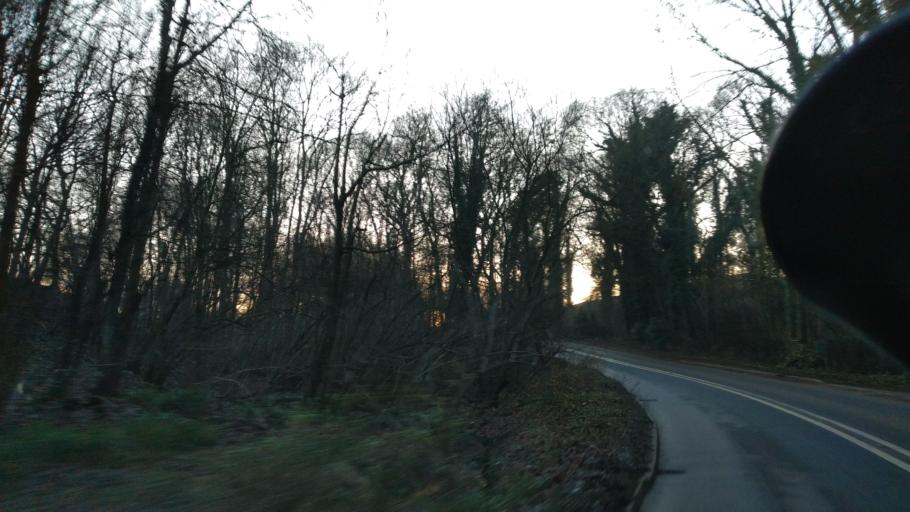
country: GB
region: England
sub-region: Wiltshire
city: Calne
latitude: 51.4098
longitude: -2.0302
